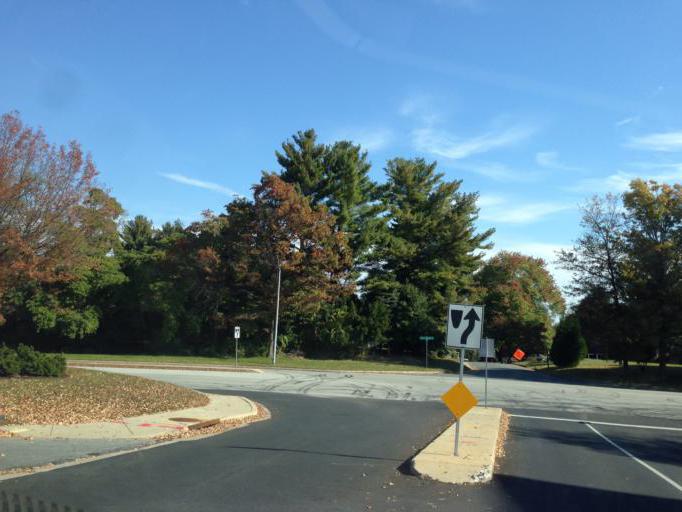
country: US
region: Maryland
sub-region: Howard County
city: Ellicott City
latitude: 39.2760
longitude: -76.8064
